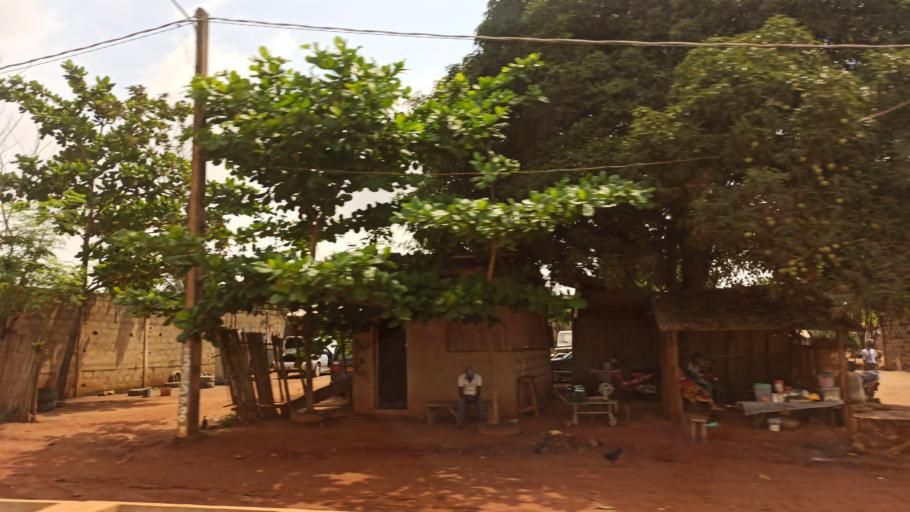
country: BJ
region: Queme
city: Porto-Novo
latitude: 6.4953
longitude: 2.5901
